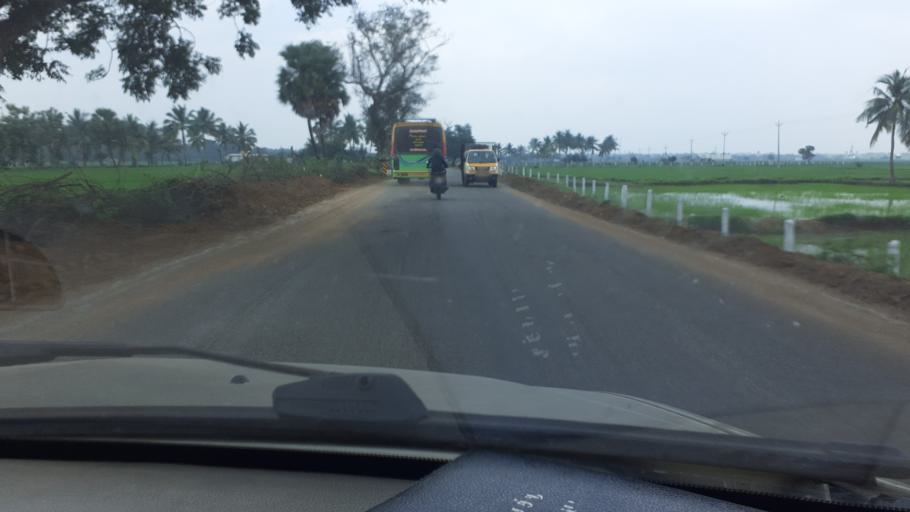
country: IN
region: Tamil Nadu
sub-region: Tirunelveli Kattabo
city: Viravanallur
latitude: 8.7259
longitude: 77.5386
